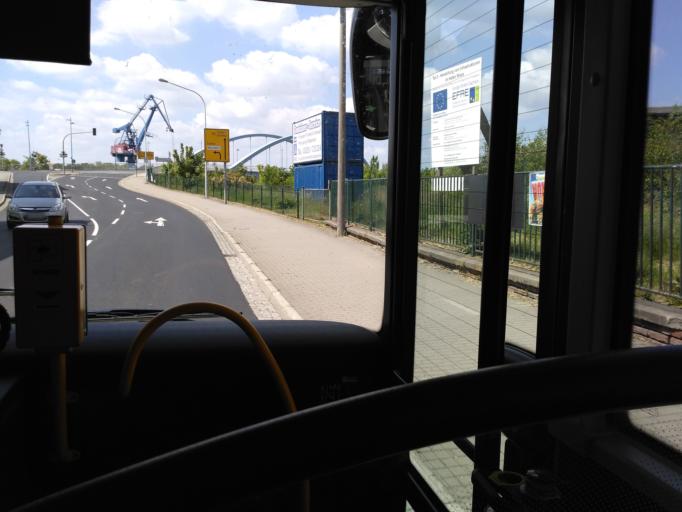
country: DE
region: Saxony
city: Riesa
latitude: 51.3181
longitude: 13.2820
